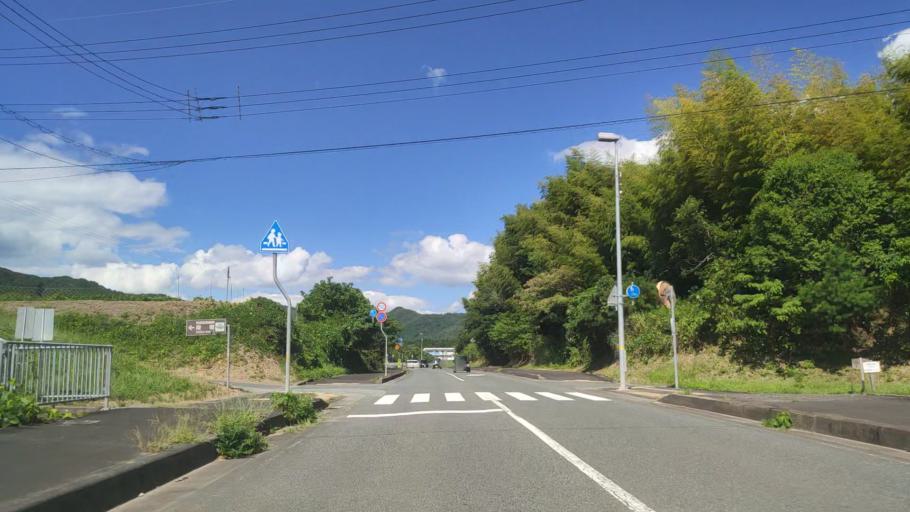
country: JP
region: Kyoto
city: Fukuchiyama
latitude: 35.2317
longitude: 135.1282
